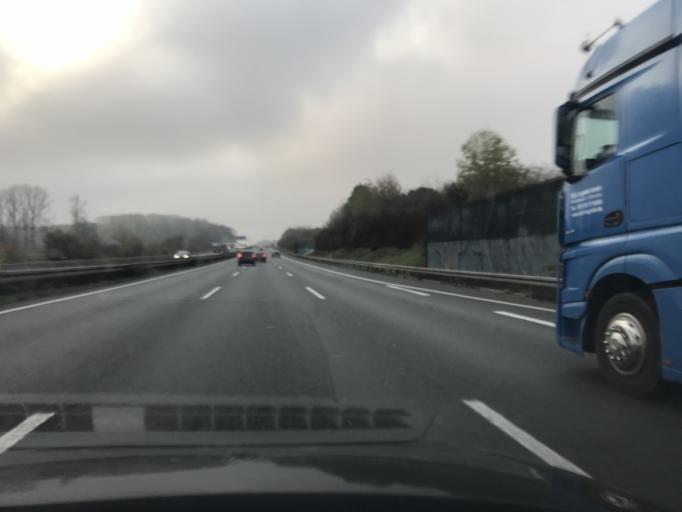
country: DE
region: North Rhine-Westphalia
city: Oelde
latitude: 51.8063
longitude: 8.1273
